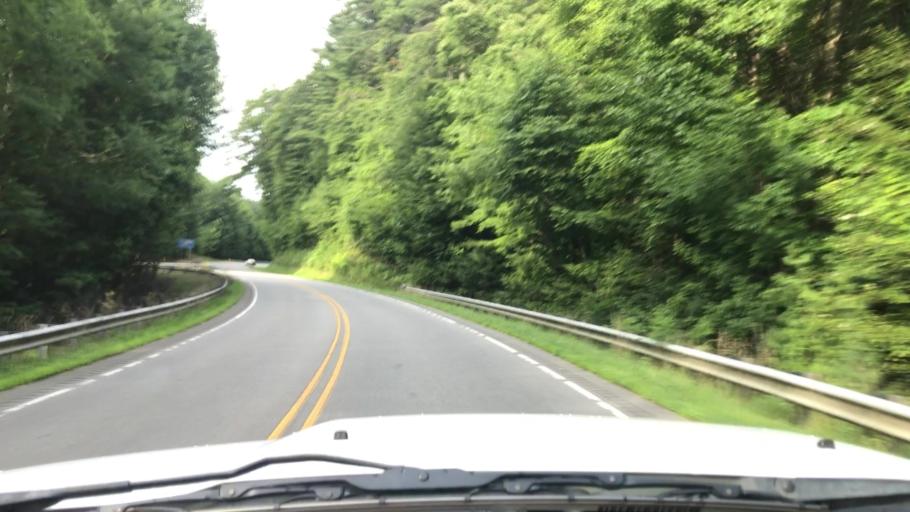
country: US
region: North Carolina
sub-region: Graham County
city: Robbinsville
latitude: 35.2701
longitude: -83.6977
